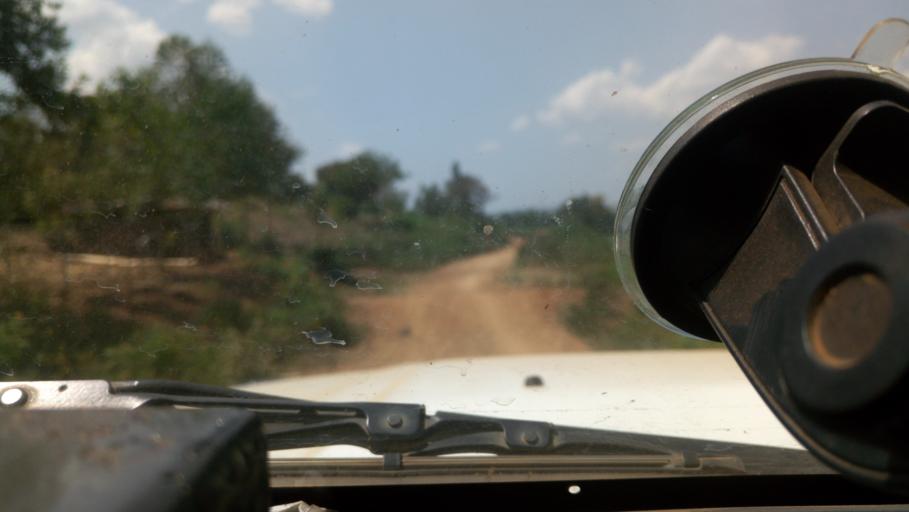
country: KE
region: Migori
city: Migori
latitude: -0.9411
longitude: 34.4410
